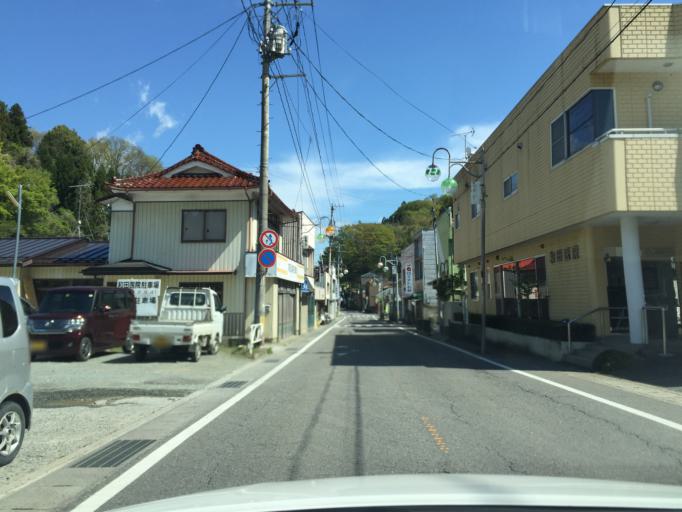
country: JP
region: Fukushima
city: Nihommatsu
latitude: 37.5613
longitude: 140.5080
